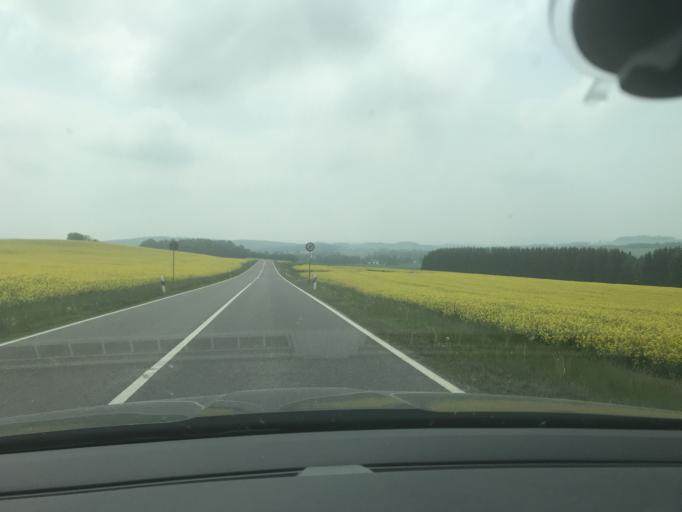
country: DE
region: Saxony
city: Grosshartmannsdorf
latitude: 50.7763
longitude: 13.3205
